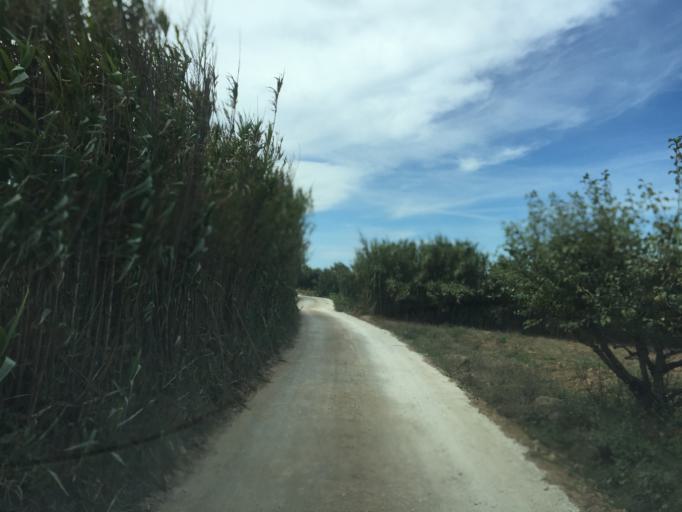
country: PT
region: Lisbon
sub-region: Lourinha
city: Lourinha
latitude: 39.1938
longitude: -9.3399
